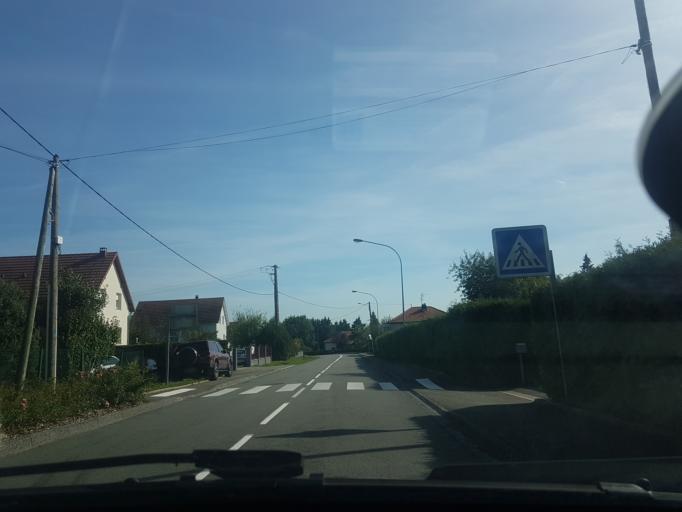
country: FR
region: Franche-Comte
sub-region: Territoire de Belfort
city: Offemont
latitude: 47.6687
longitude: 6.9111
